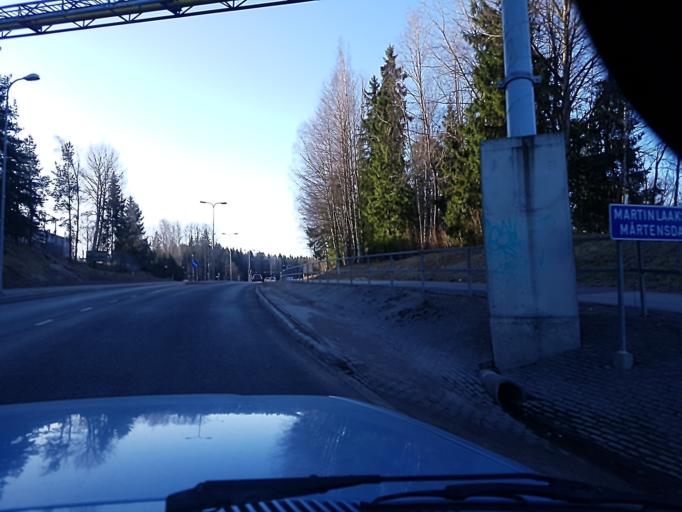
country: FI
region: Uusimaa
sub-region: Helsinki
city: Kilo
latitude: 60.2834
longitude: 24.8345
